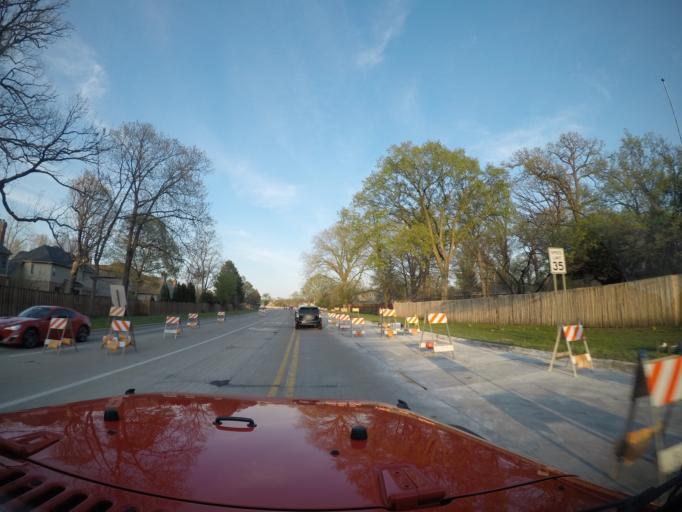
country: US
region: Illinois
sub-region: Cook County
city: Des Plaines
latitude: 42.0867
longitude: -87.8772
